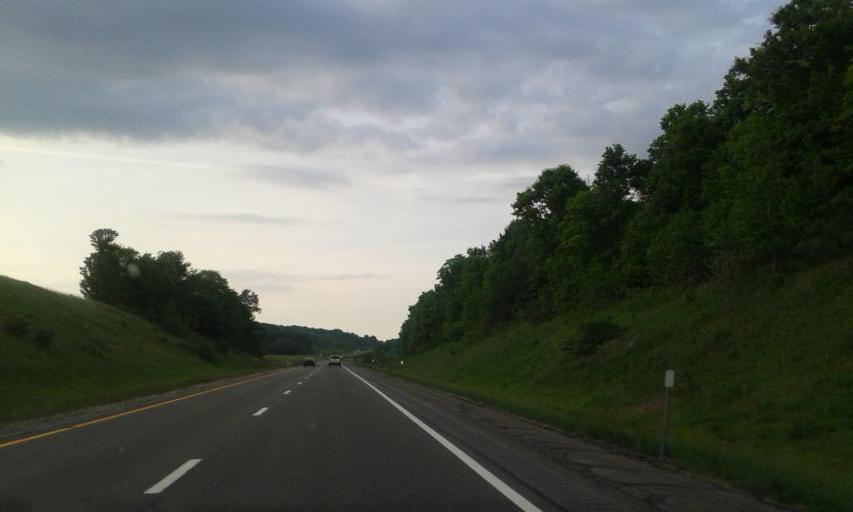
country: US
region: New York
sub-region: Broome County
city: Chenango Bridge
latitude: 42.2430
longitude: -75.9166
